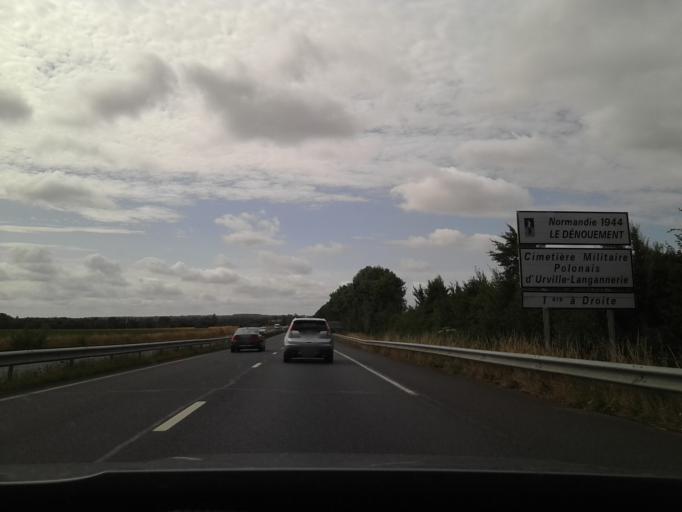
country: FR
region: Lower Normandy
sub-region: Departement du Calvados
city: Bretteville-sur-Laize
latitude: 49.0324
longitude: -0.2745
